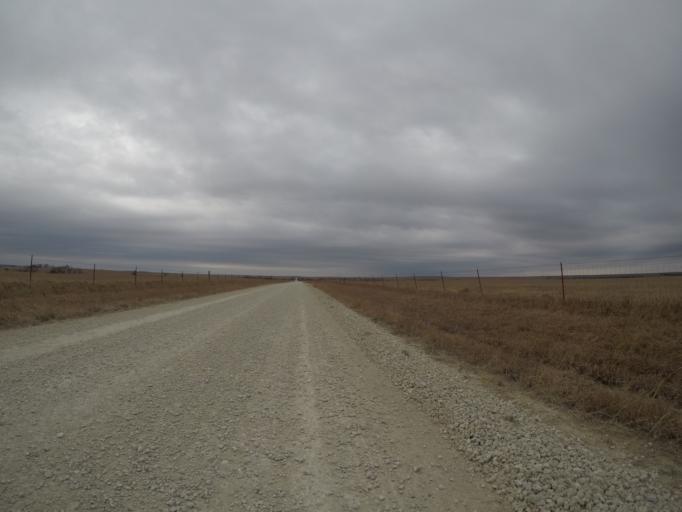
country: US
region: Kansas
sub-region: Wabaunsee County
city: Alma
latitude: 38.7855
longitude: -96.1500
